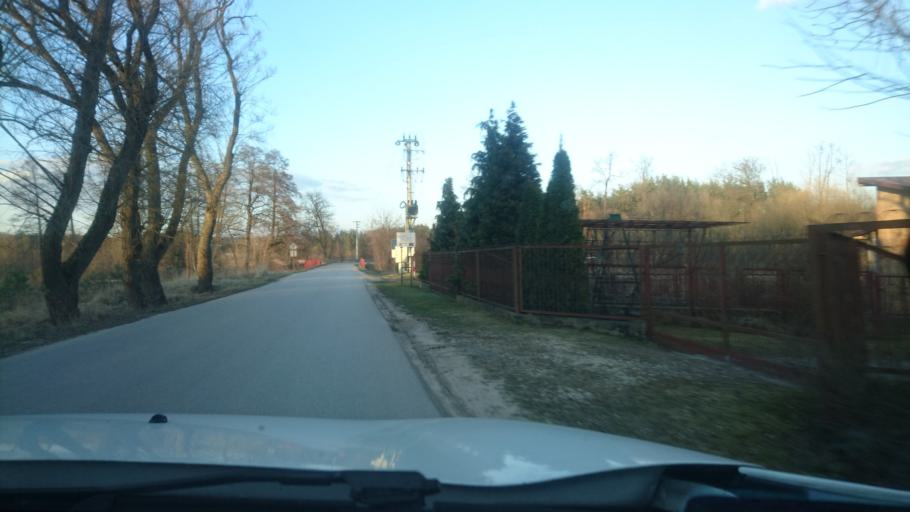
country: PL
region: Swietokrzyskie
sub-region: Powiat kielecki
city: Pierzchnica
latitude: 50.7770
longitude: 20.7081
